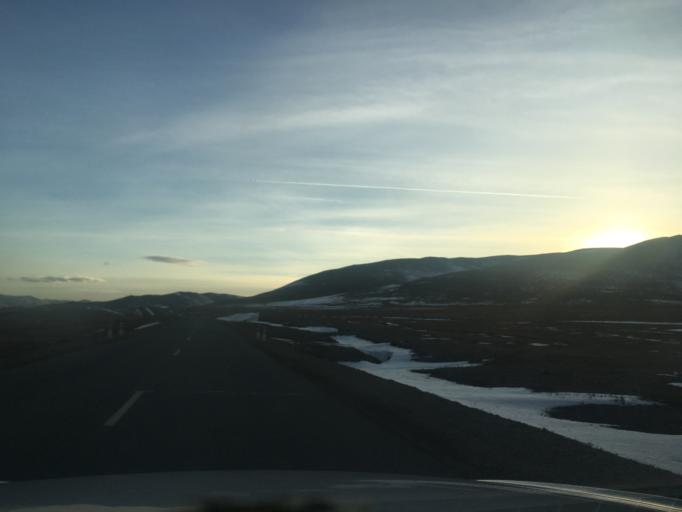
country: MN
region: Central Aimak
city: Mandal
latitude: 48.2296
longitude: 106.7182
